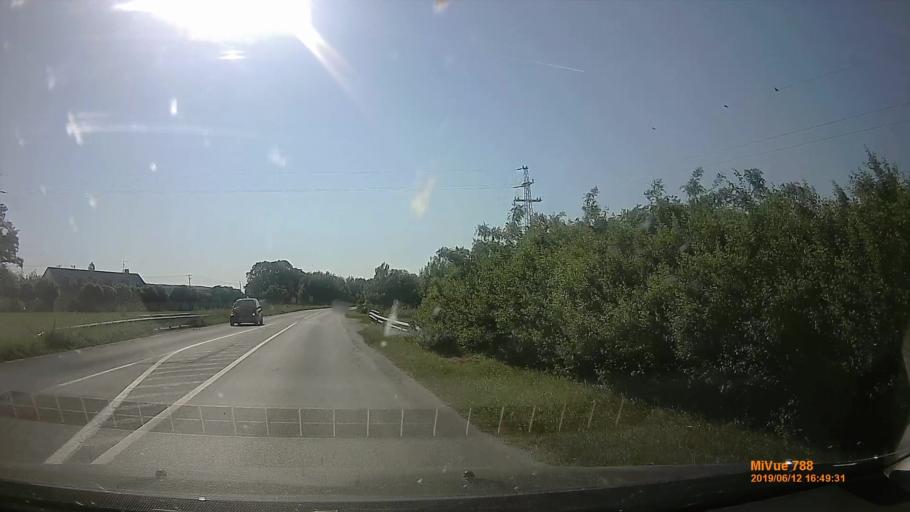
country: HU
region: Csongrad
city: Kiszombor
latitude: 46.1938
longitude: 20.4094
